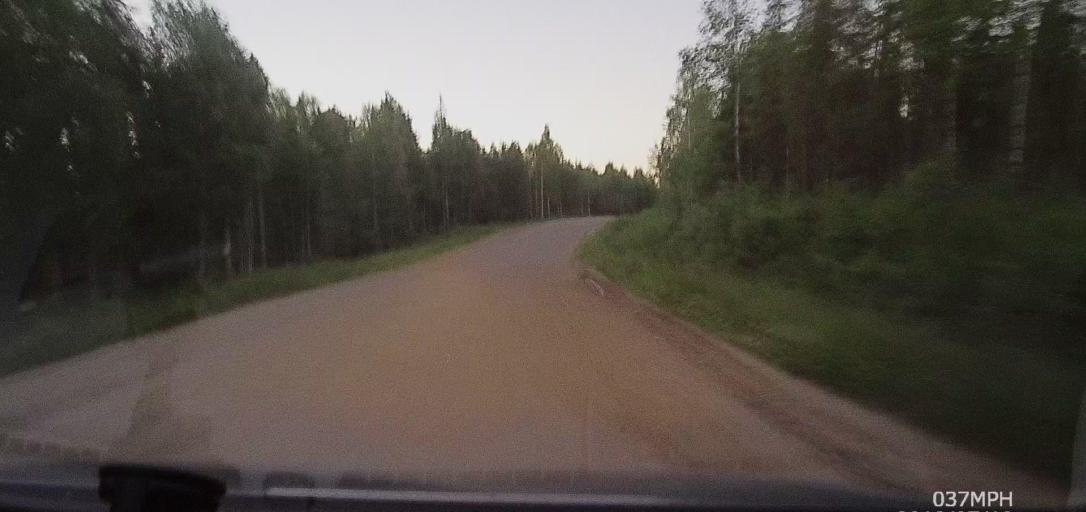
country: RU
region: Arkhangelskaya
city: Pinega
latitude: 64.4321
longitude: 43.1282
